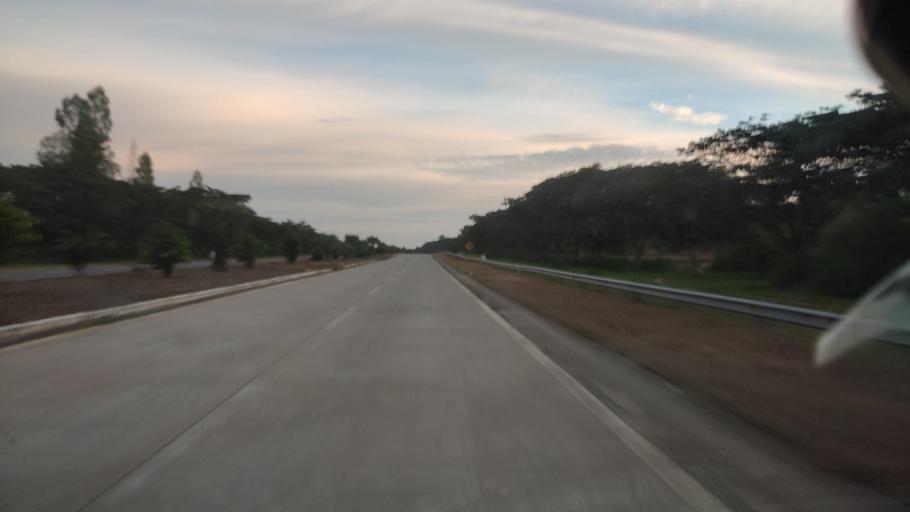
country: MM
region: Mandalay
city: Yamethin
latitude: 20.2654
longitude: 95.8905
